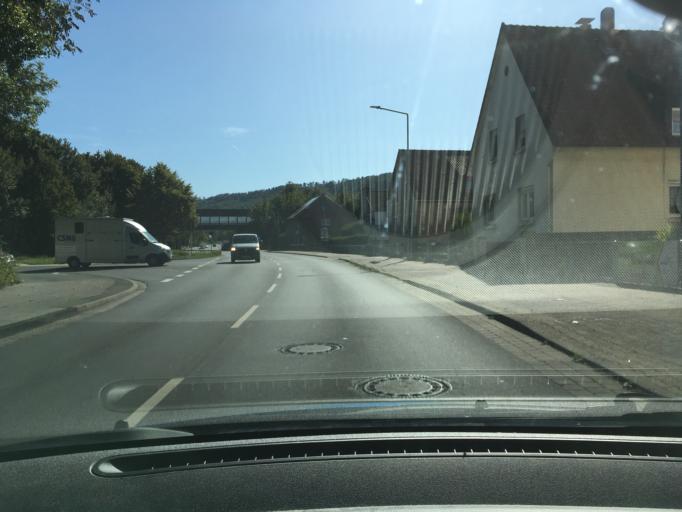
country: DE
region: Lower Saxony
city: Springe
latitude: 52.2052
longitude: 9.5556
